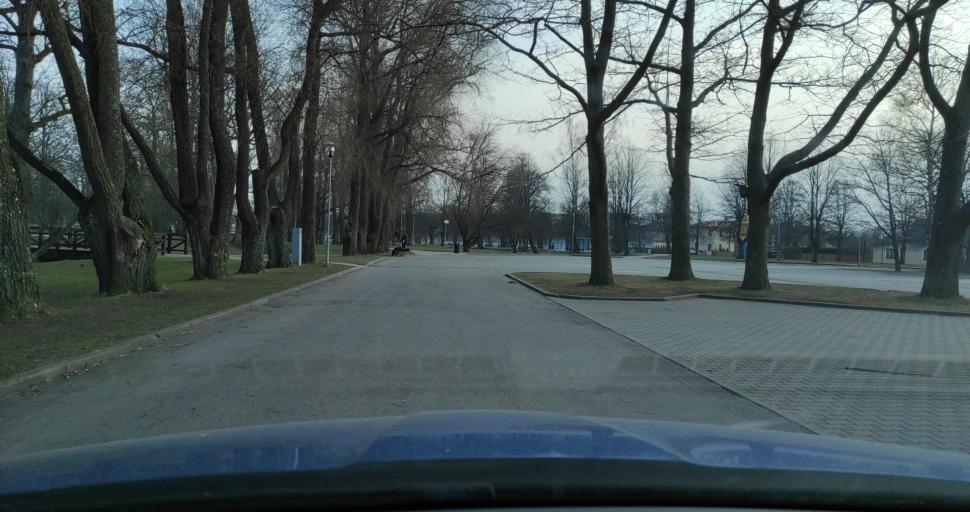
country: LV
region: Ventspils
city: Ventspils
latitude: 57.3860
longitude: 21.5677
